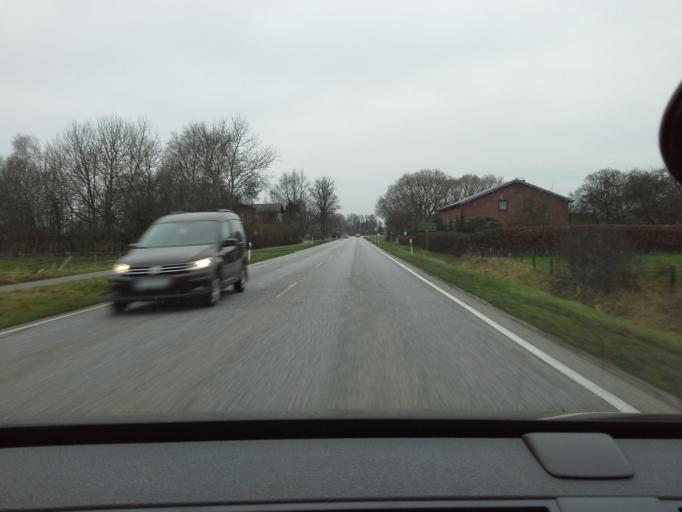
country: DE
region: Schleswig-Holstein
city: Bilsen
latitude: 53.7813
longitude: 9.8750
